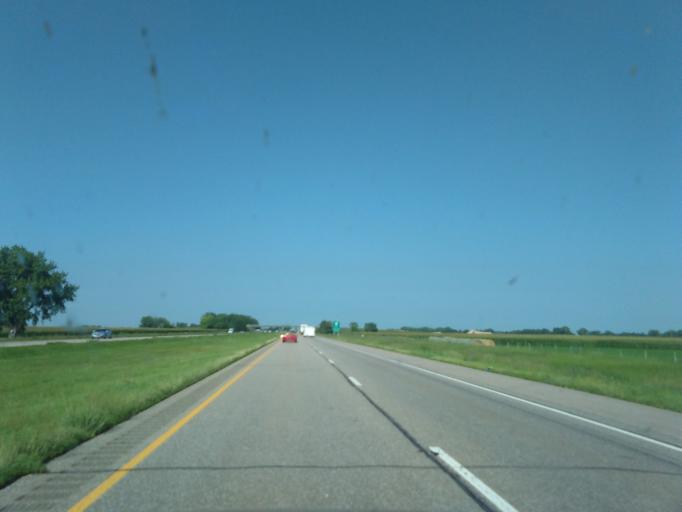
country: US
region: Nebraska
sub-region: Hall County
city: Wood River
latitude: 40.7897
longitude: -98.5186
